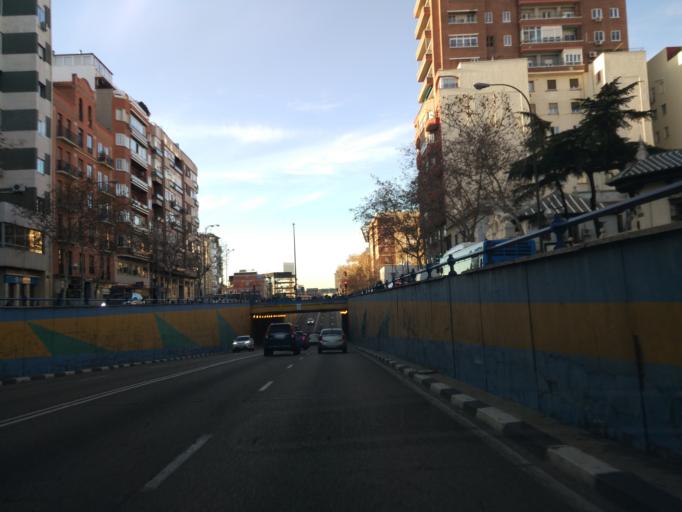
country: ES
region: Madrid
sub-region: Provincia de Madrid
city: Salamanca
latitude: 40.4366
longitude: -3.6765
